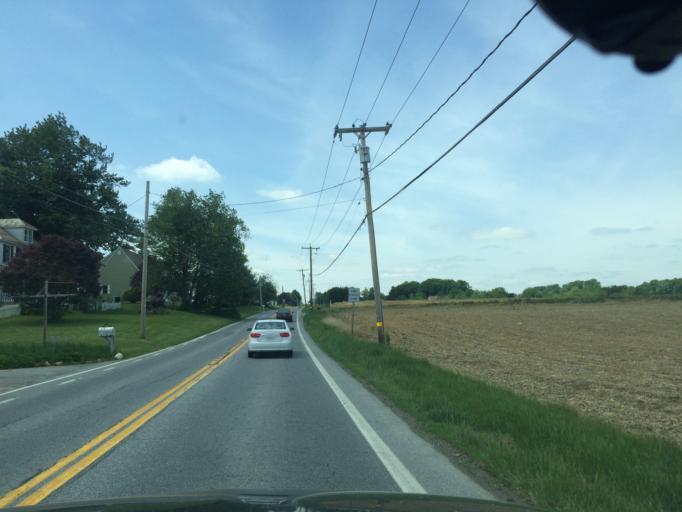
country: US
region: Maryland
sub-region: Carroll County
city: Eldersburg
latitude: 39.4702
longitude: -76.9437
